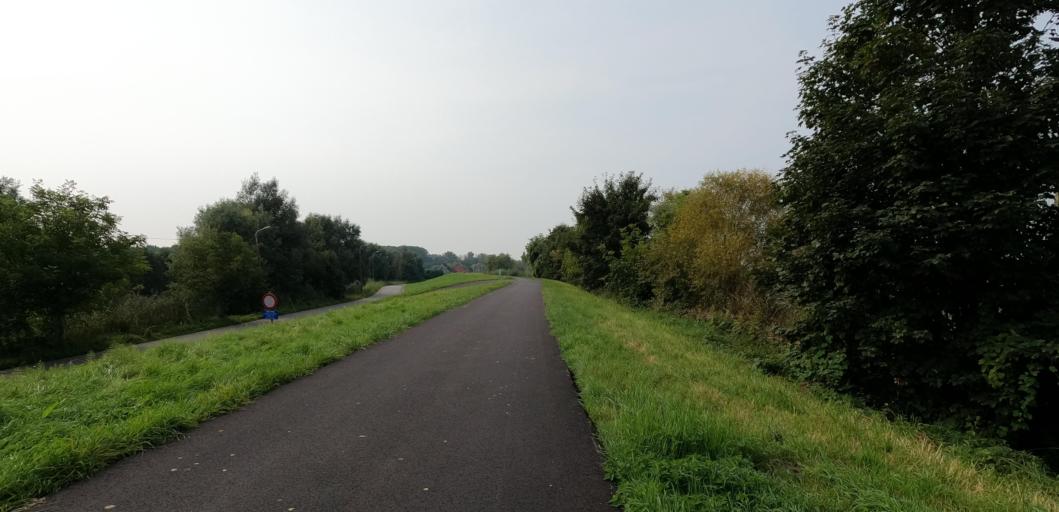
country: BE
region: Flanders
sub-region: Provincie Oost-Vlaanderen
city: Temse
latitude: 51.1118
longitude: 4.2010
